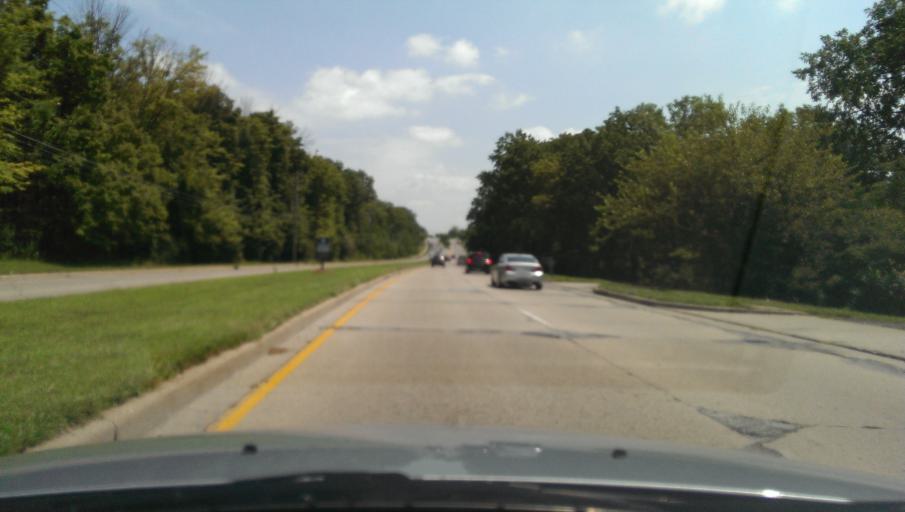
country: US
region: Indiana
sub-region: Marion County
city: Lawrence
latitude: 39.8550
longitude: -86.0309
